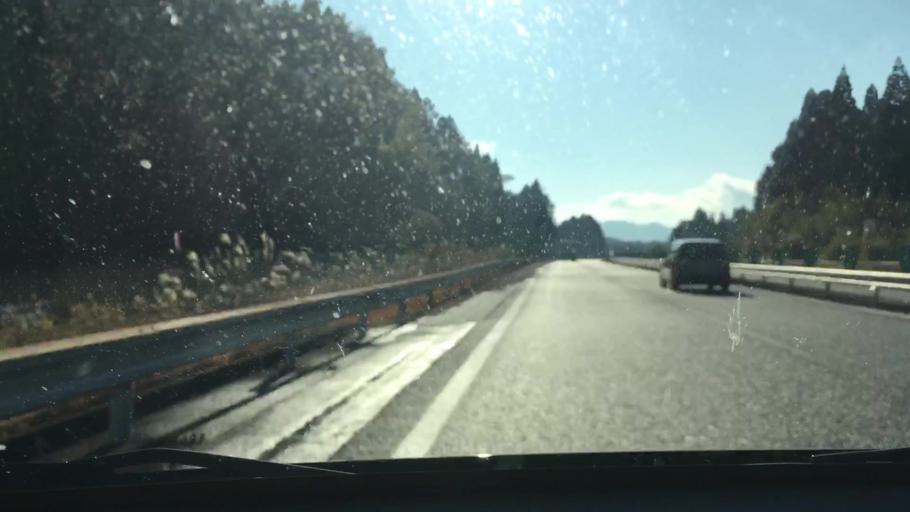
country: JP
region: Kagoshima
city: Okuchi-shinohara
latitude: 32.0197
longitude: 130.7726
